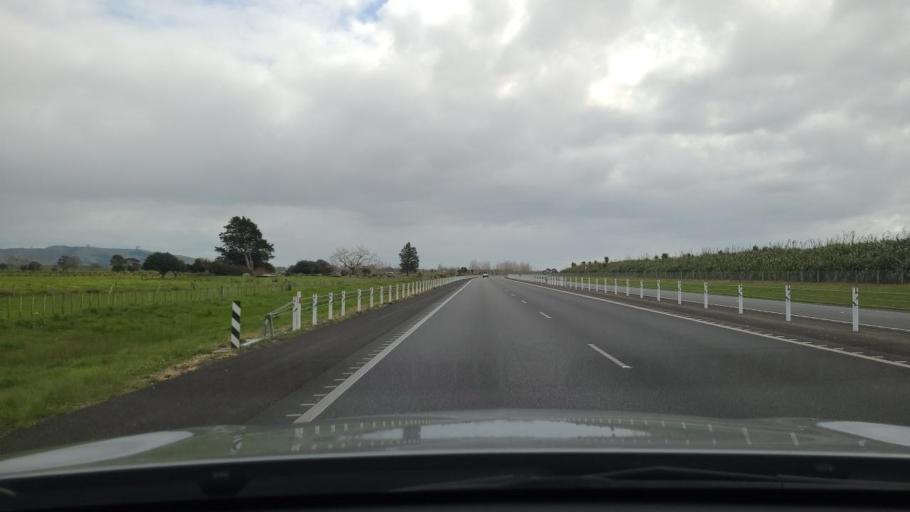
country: NZ
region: Bay of Plenty
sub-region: Western Bay of Plenty District
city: Maketu
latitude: -37.7555
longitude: 176.3625
